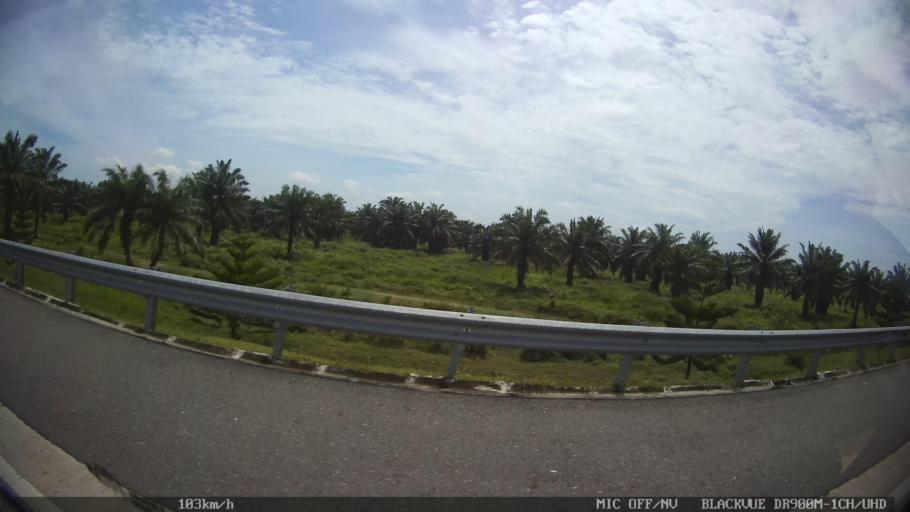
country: ID
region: North Sumatra
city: Percut
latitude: 3.5921
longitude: 98.8443
